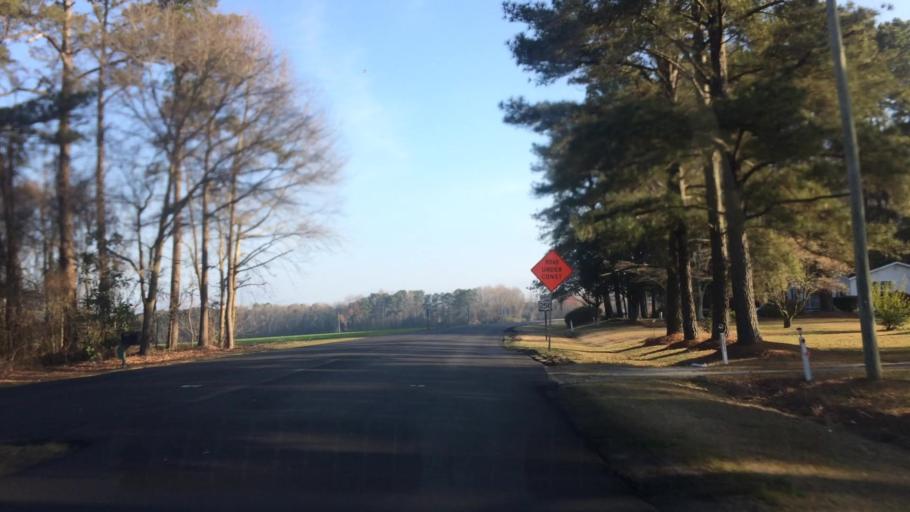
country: US
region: North Carolina
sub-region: Edgecombe County
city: Pinetops
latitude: 35.6851
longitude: -77.6438
